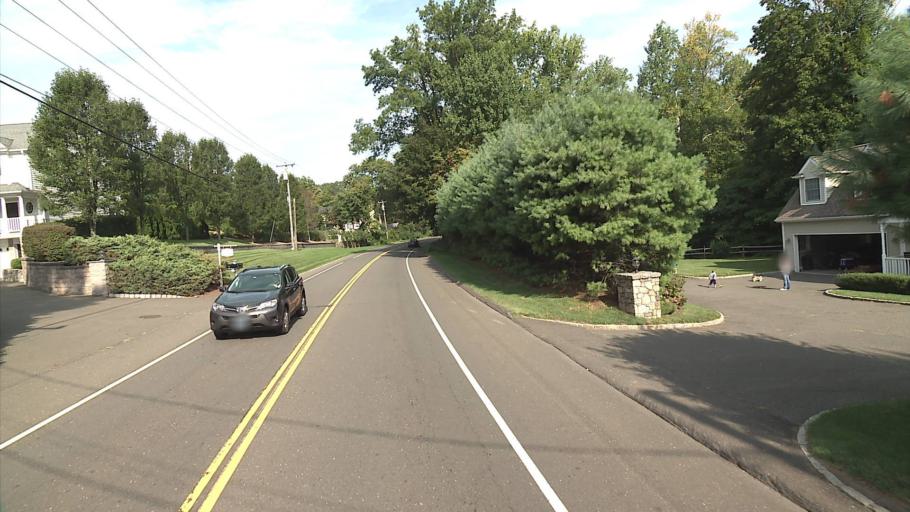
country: US
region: Connecticut
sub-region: Fairfield County
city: New Canaan
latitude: 41.1526
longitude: -73.4916
